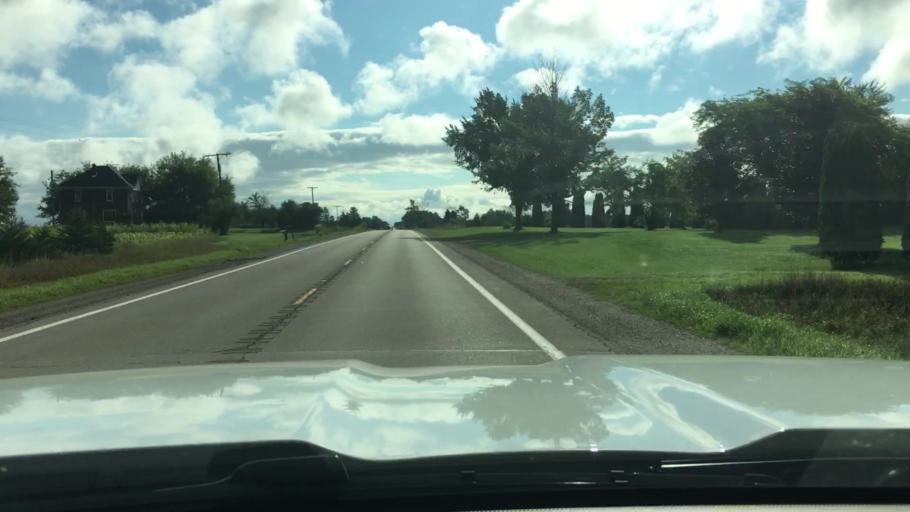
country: US
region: Michigan
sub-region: Tuscola County
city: Cass City
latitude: 43.5995
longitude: -83.2419
